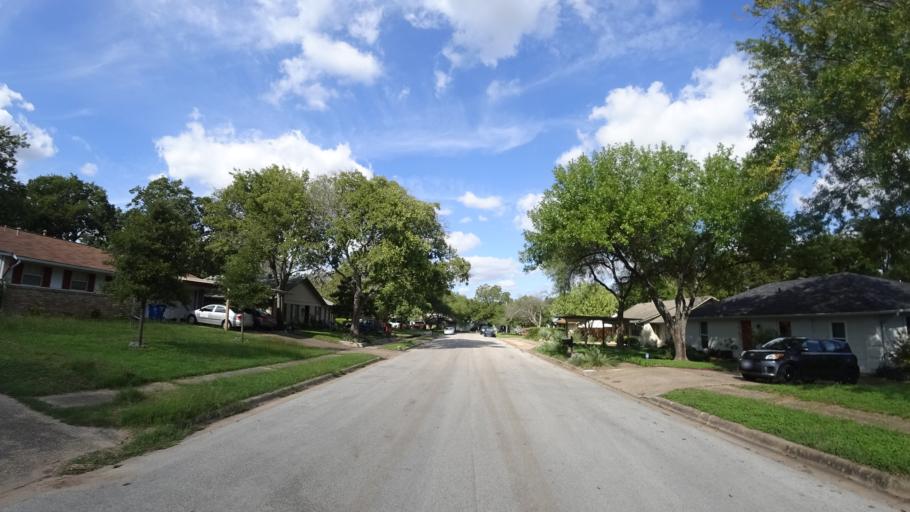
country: US
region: Texas
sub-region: Travis County
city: Onion Creek
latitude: 30.2002
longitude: -97.7890
